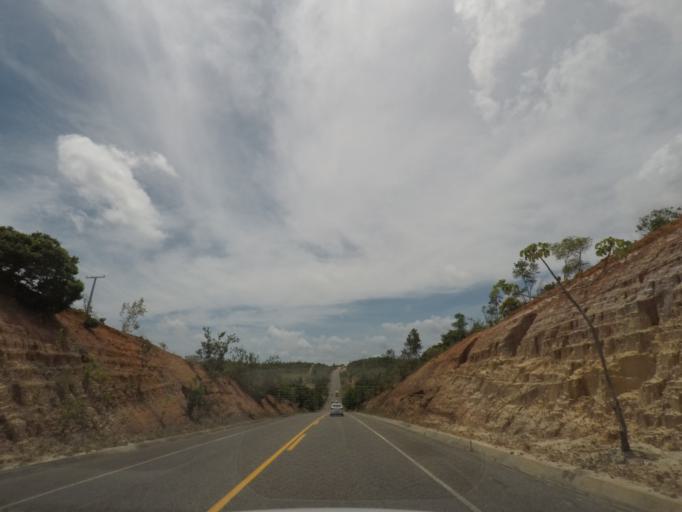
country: BR
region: Bahia
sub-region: Conde
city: Conde
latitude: -11.9205
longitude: -37.6646
